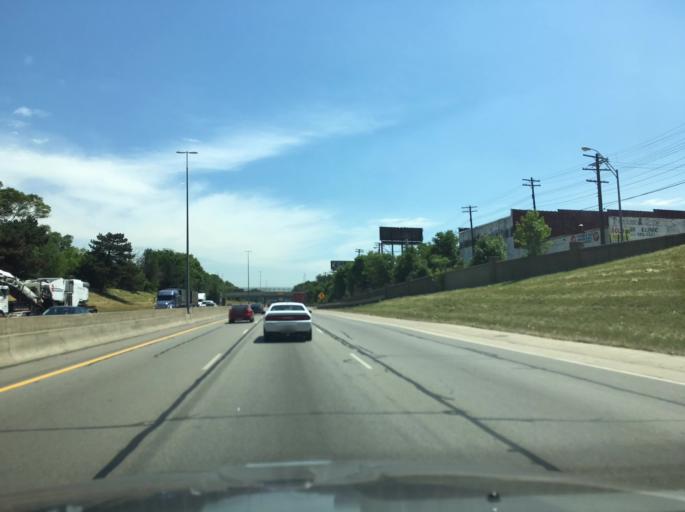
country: US
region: Michigan
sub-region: Wayne County
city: Dearborn
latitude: 42.3293
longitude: -83.1541
